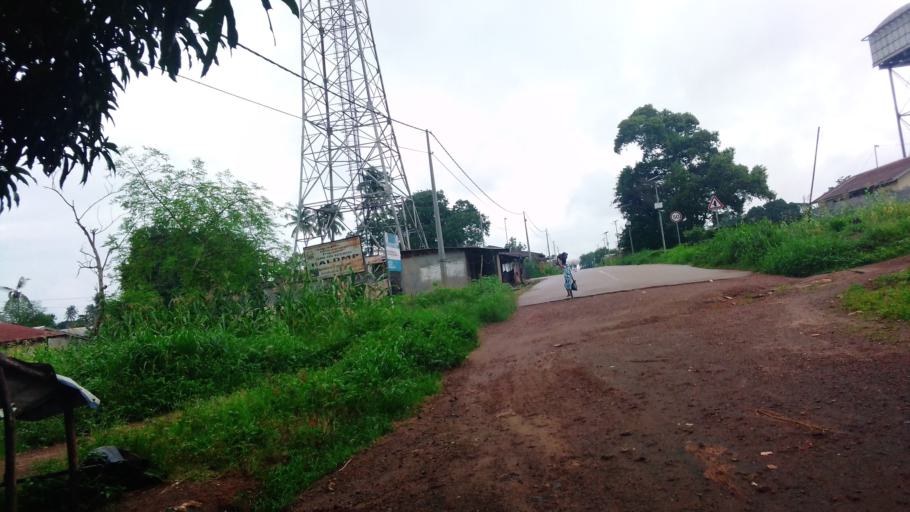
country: SL
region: Northern Province
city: Lunsar
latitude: 8.6852
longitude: -12.5284
